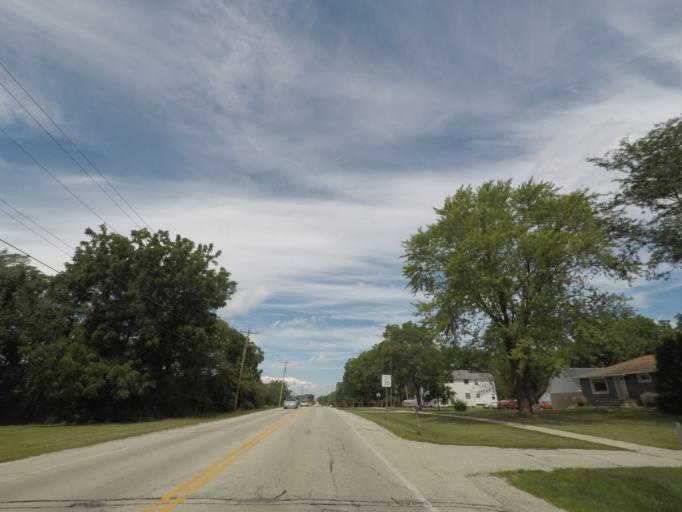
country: US
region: Wisconsin
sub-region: Milwaukee County
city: Greendale
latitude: 42.9125
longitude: -87.9796
